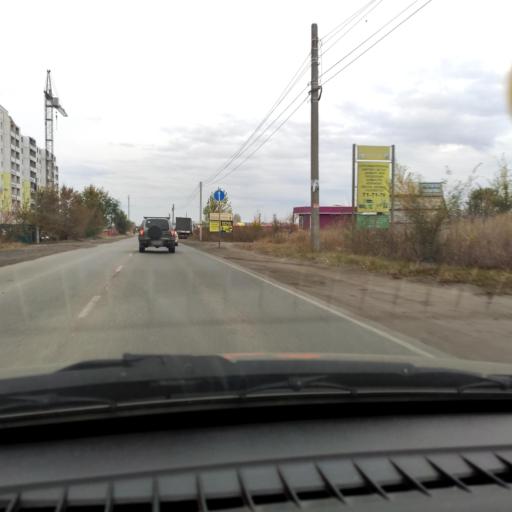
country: RU
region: Samara
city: Tol'yatti
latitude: 53.5086
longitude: 49.2513
